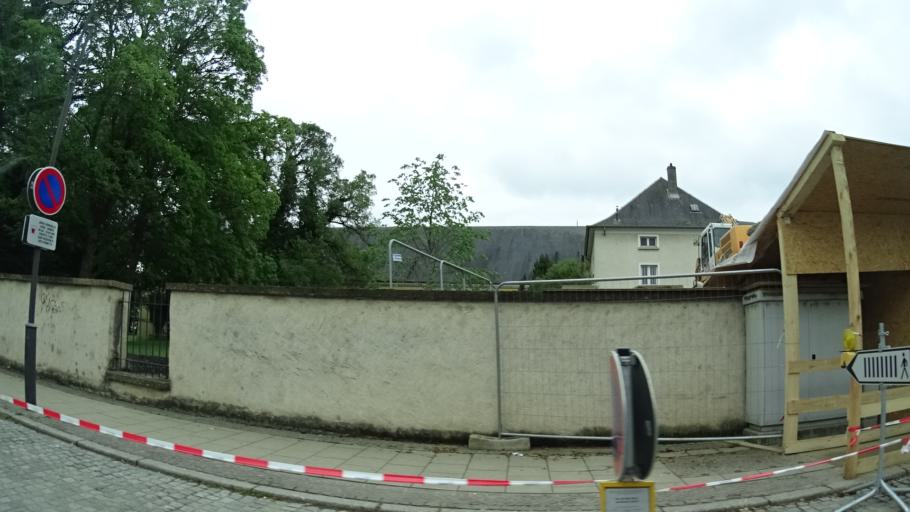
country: LU
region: Luxembourg
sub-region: Canton d'Esch-sur-Alzette
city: Bettembourg
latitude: 49.5179
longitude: 6.0961
